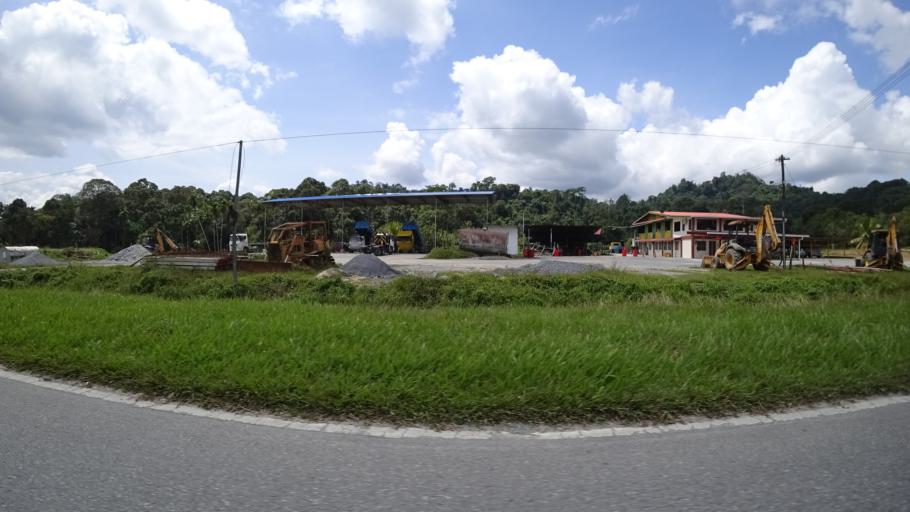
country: BN
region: Tutong
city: Tutong
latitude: 4.6851
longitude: 114.8090
